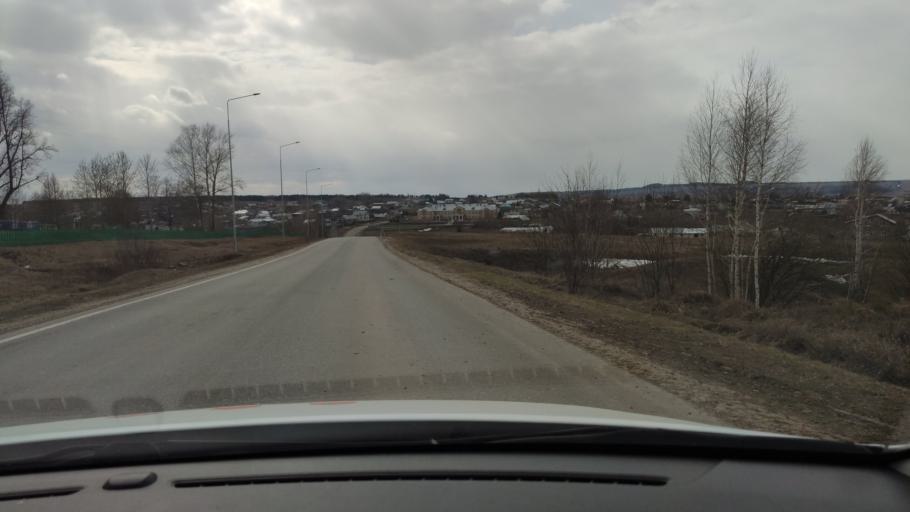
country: RU
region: Tatarstan
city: Vysokaya Gora
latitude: 56.2192
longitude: 49.2688
